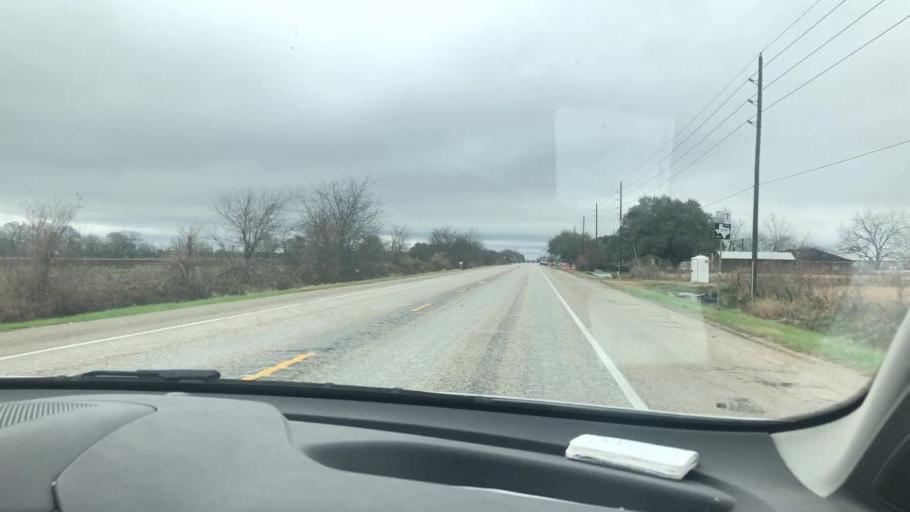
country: US
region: Texas
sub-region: Wharton County
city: Wharton
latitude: 29.2669
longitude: -96.0579
